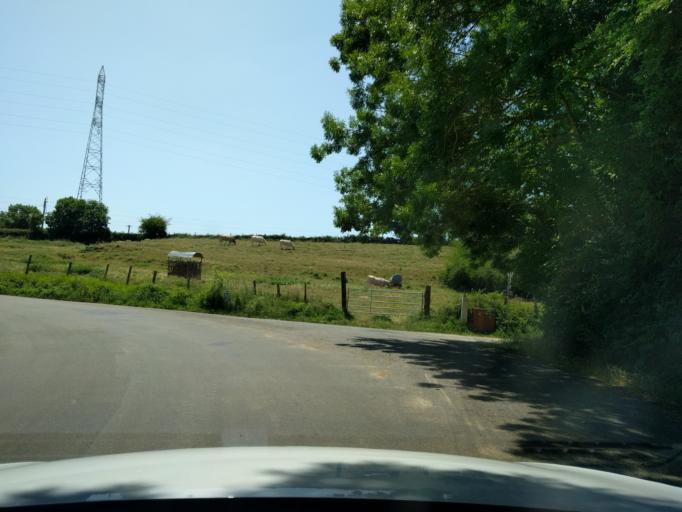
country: FR
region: Poitou-Charentes
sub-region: Departement des Deux-Sevres
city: Niort
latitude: 46.3549
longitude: -0.4575
